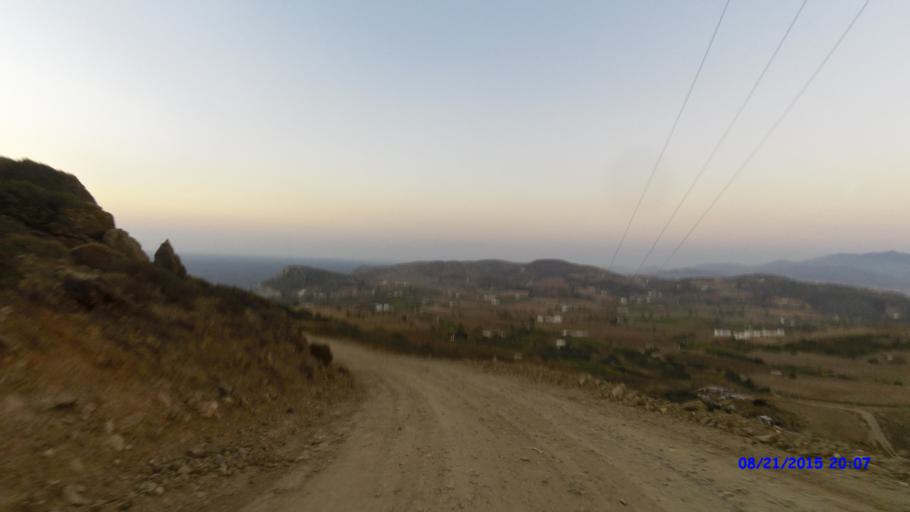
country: GR
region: South Aegean
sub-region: Nomos Kykladon
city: Antiparos
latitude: 37.0076
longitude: 25.0457
